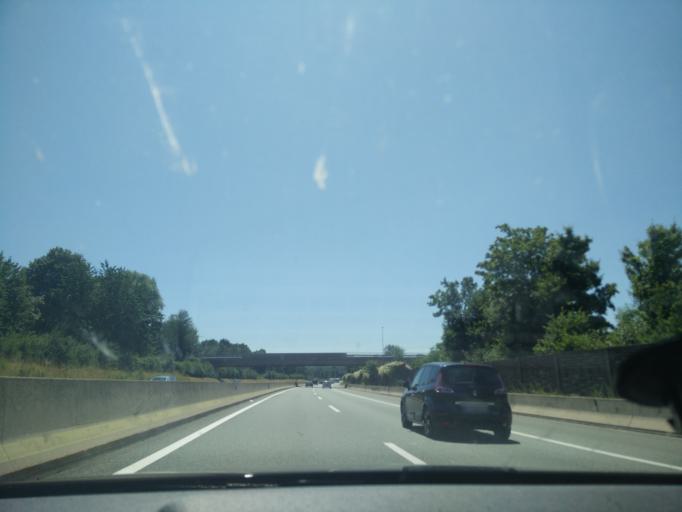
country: AT
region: Styria
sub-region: Politischer Bezirk Hartberg-Fuerstenfeld
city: Sebersdorf
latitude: 47.1886
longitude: 15.9965
